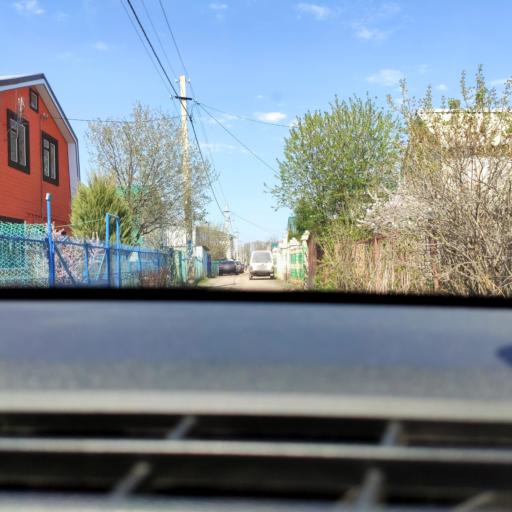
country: RU
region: Samara
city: Tol'yatti
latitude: 53.5951
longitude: 49.3012
